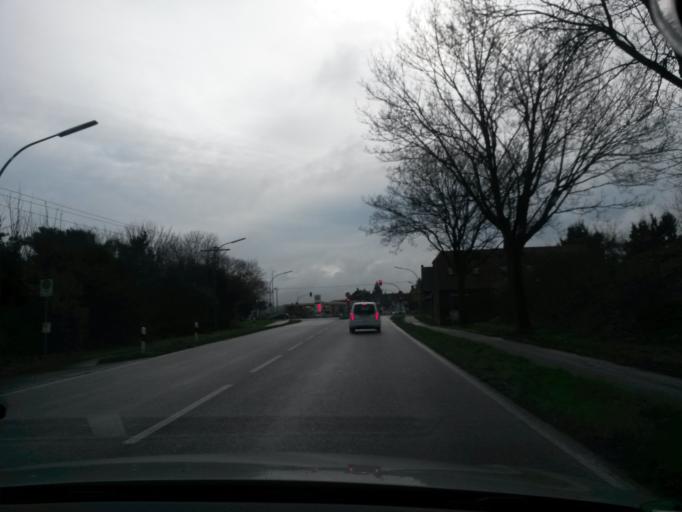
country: DE
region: North Rhine-Westphalia
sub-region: Regierungsbezirk Dusseldorf
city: Kamp-Lintfort
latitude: 51.5140
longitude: 6.5395
